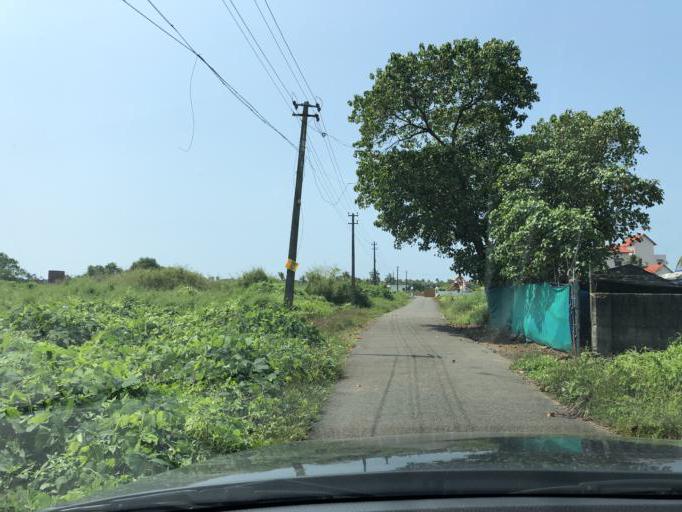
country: IN
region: Kerala
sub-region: Ernakulam
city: Cochin
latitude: 9.9964
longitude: 76.2346
